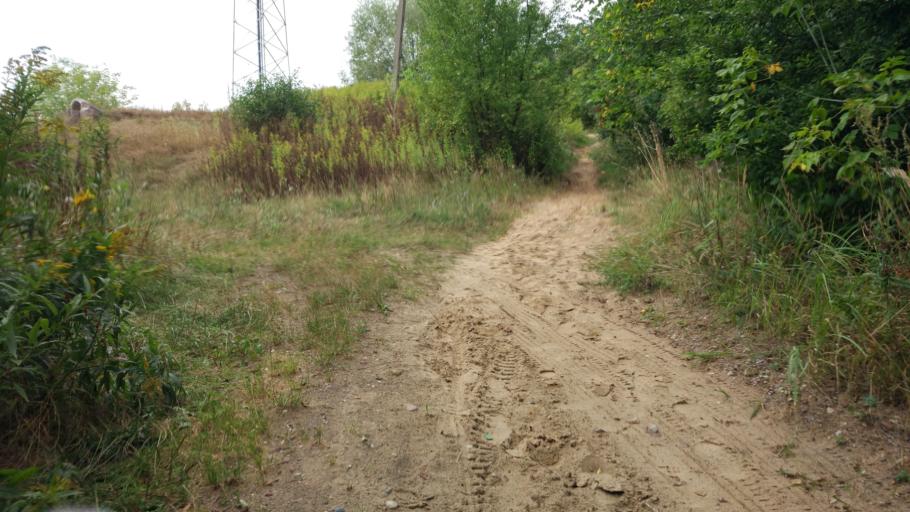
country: PL
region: Masovian Voivodeship
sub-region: Plock
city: Plock
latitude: 52.5256
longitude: 19.7490
